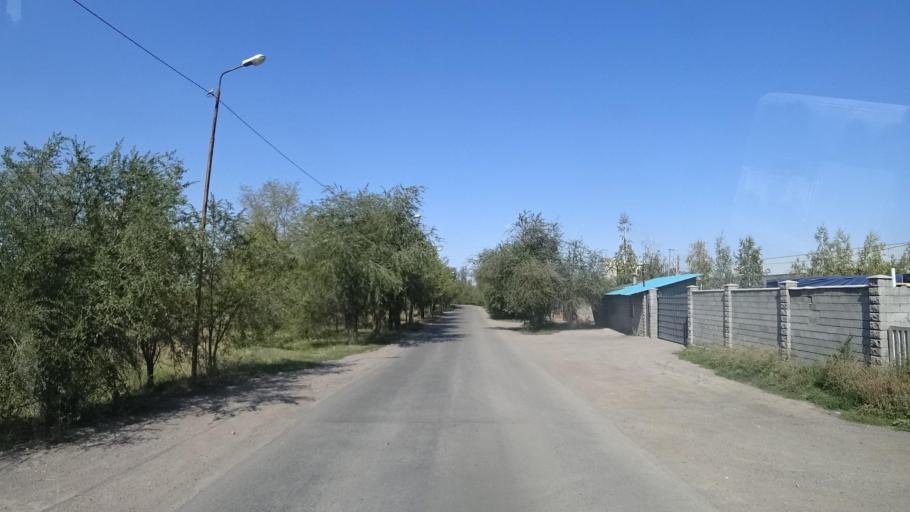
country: KZ
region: Almaty Oblysy
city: Pervomayskiy
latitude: 43.3311
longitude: 77.0013
